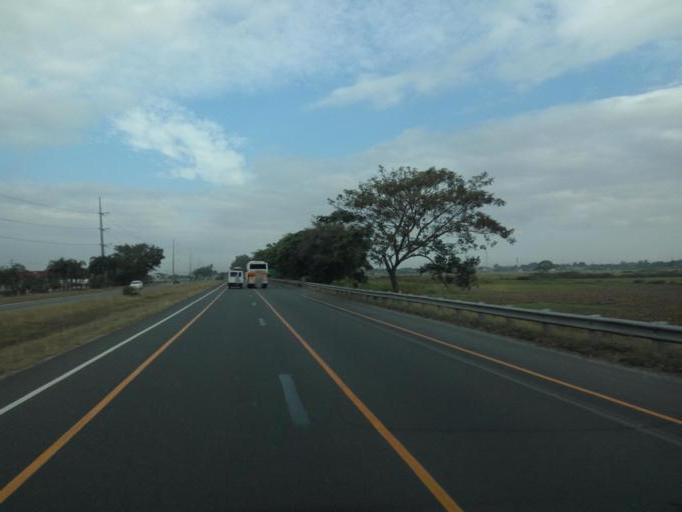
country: PH
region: Central Luzon
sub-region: Province of Pampanga
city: Pau
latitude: 15.0305
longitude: 120.7166
